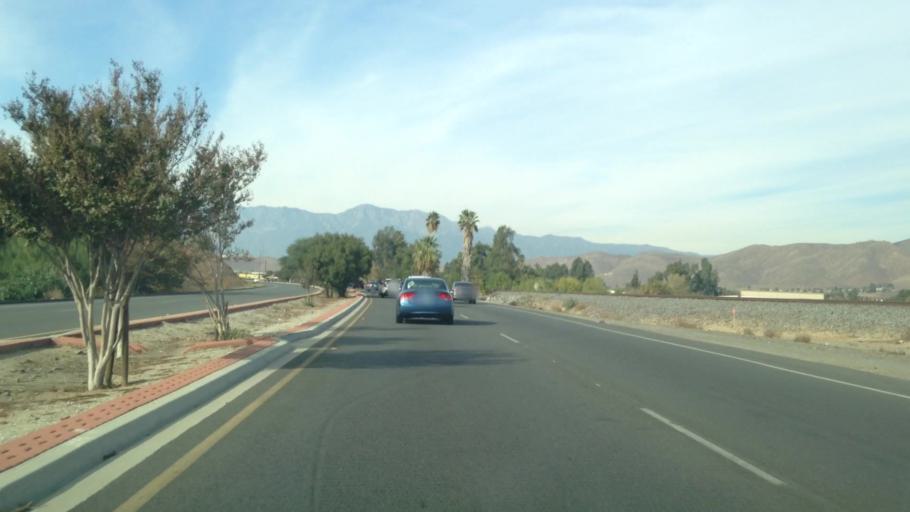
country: US
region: California
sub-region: Riverside County
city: Pedley
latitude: 33.9911
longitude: -117.4812
